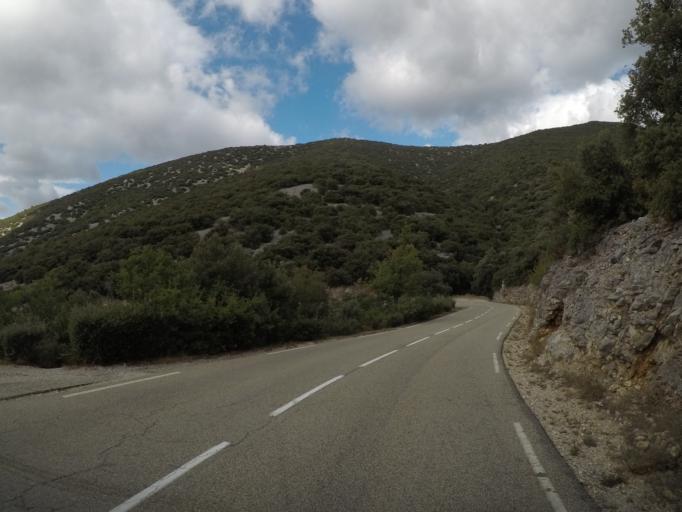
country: FR
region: Rhone-Alpes
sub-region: Departement de la Drome
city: Buis-les-Baronnies
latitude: 44.2190
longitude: 5.2283
